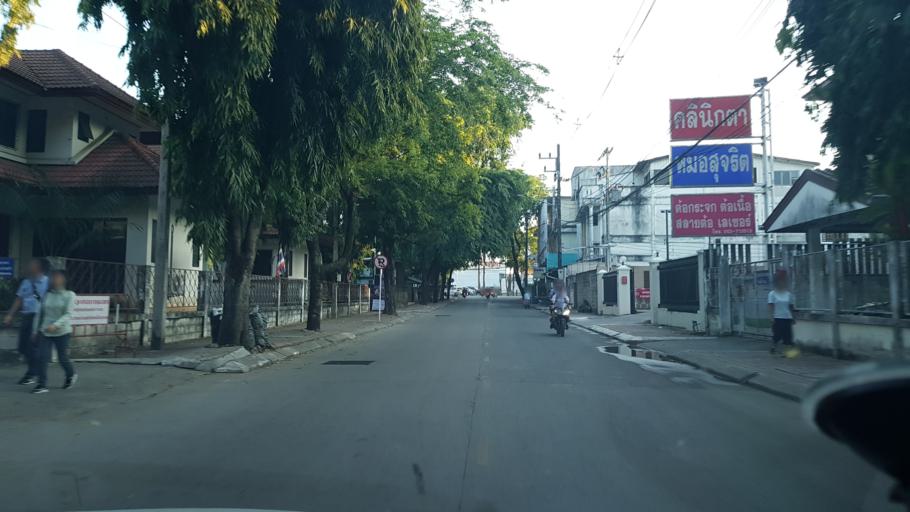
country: TH
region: Chiang Rai
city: Chiang Rai
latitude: 19.9078
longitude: 99.8354
